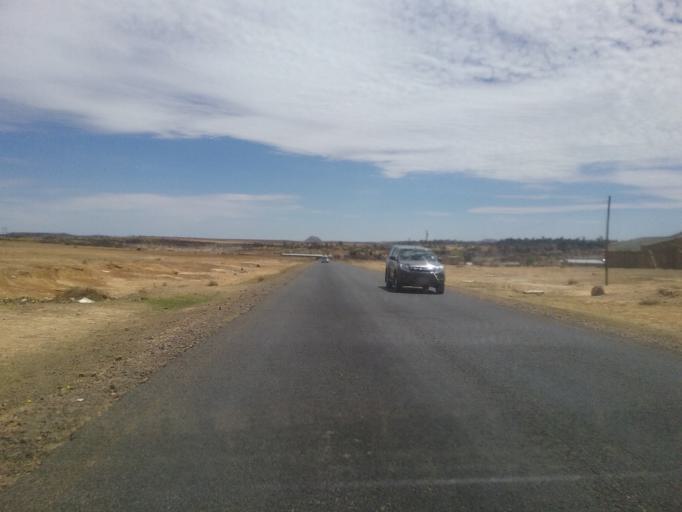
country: LS
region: Mafeteng
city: Mafeteng
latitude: -29.8546
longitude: 27.2326
